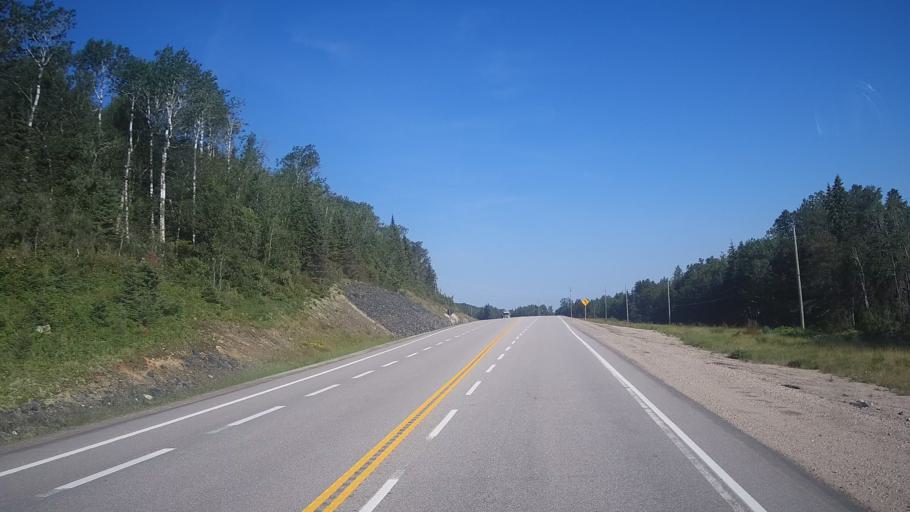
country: CA
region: Ontario
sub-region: Rainy River District
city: Atikokan
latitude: 49.4810
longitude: -91.9534
